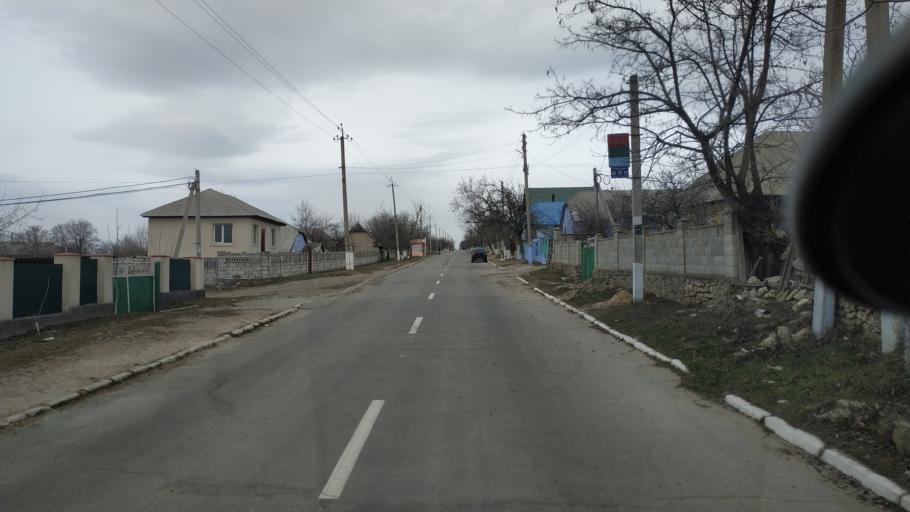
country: MD
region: Telenesti
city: Cocieri
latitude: 47.3470
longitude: 29.1177
